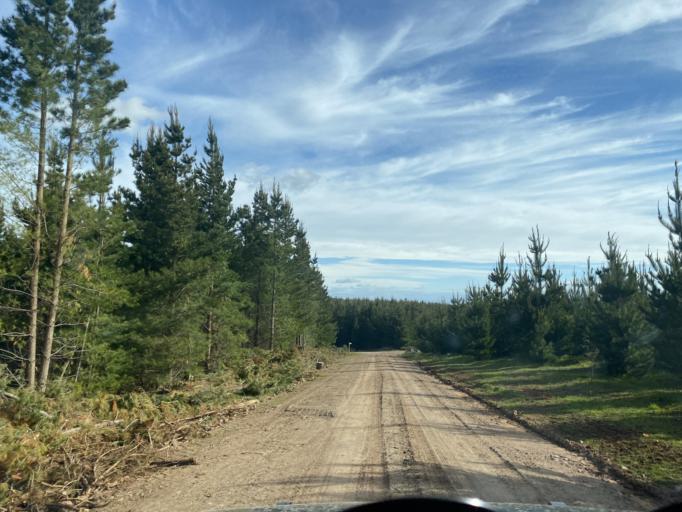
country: AU
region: Victoria
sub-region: Mansfield
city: Mansfield
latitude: -36.8346
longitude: 146.1788
